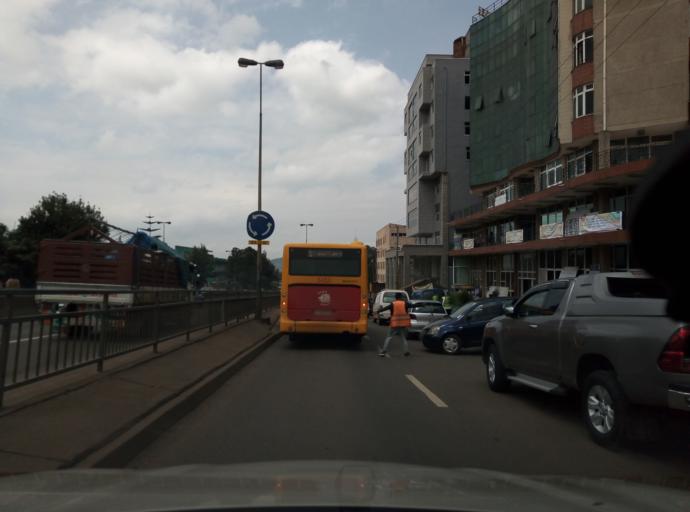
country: ET
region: Adis Abeba
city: Addis Ababa
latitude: 8.9980
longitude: 38.7186
